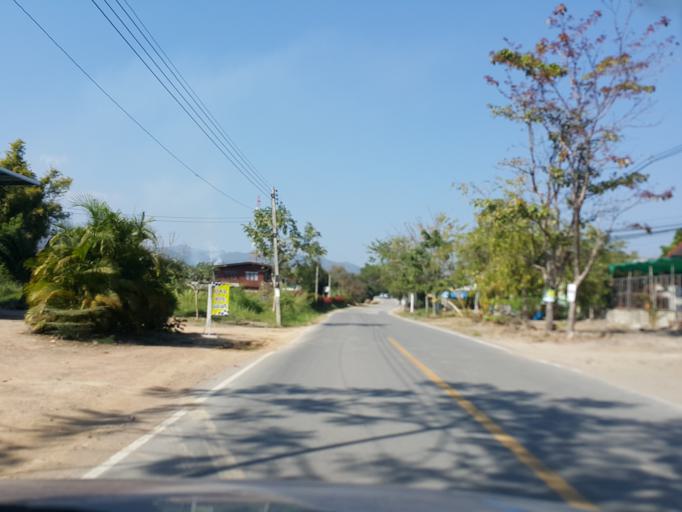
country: TH
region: Chiang Mai
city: Mae Wang
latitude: 18.6102
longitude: 98.7809
